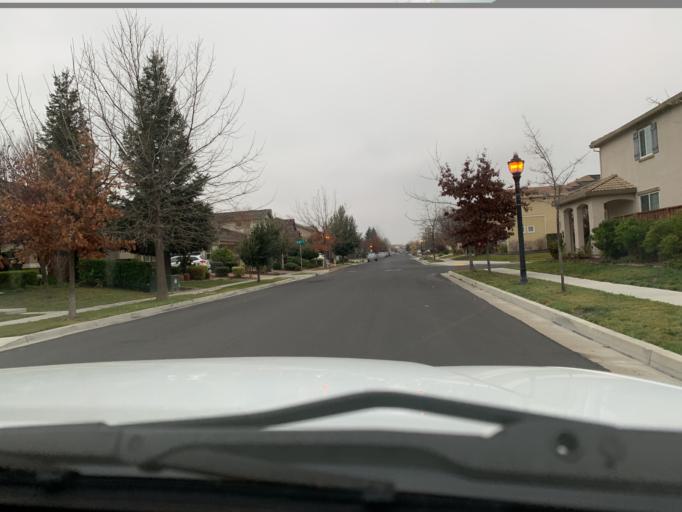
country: US
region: California
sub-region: Yolo County
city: Woodland
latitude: 38.6468
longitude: -121.7388
